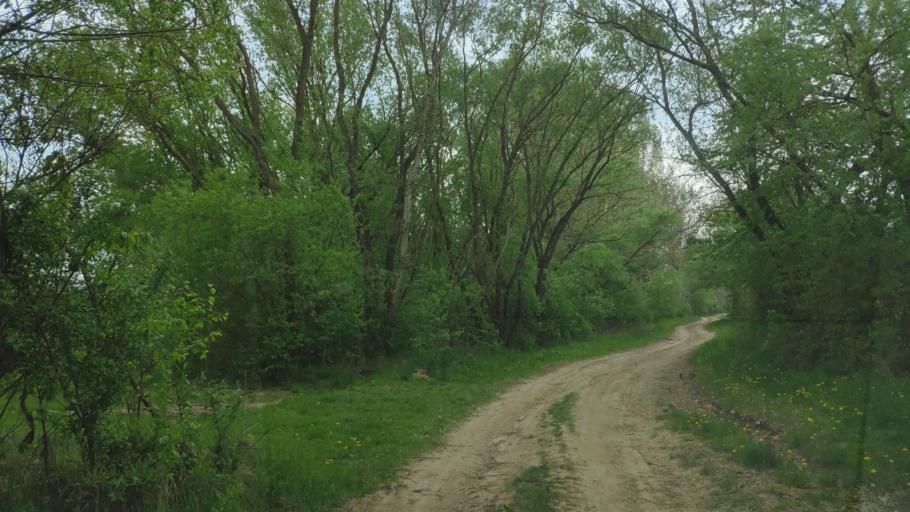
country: SK
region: Kosicky
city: Moldava nad Bodvou
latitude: 48.6116
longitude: 21.0395
